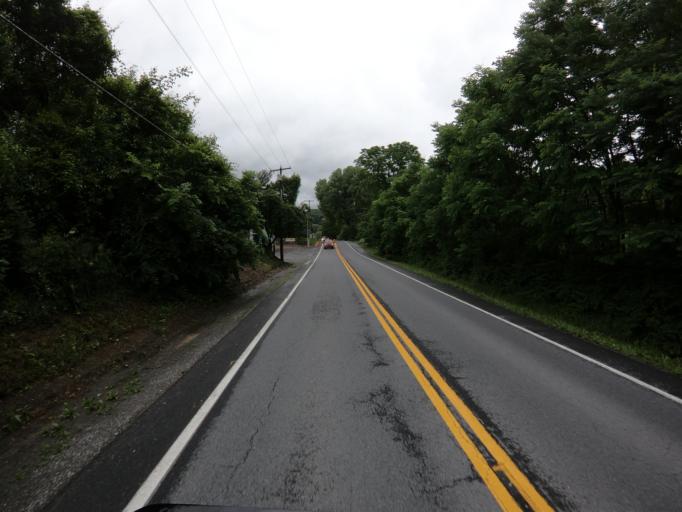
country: US
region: Maryland
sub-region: Washington County
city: Boonsboro
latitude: 39.4948
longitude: -77.6422
